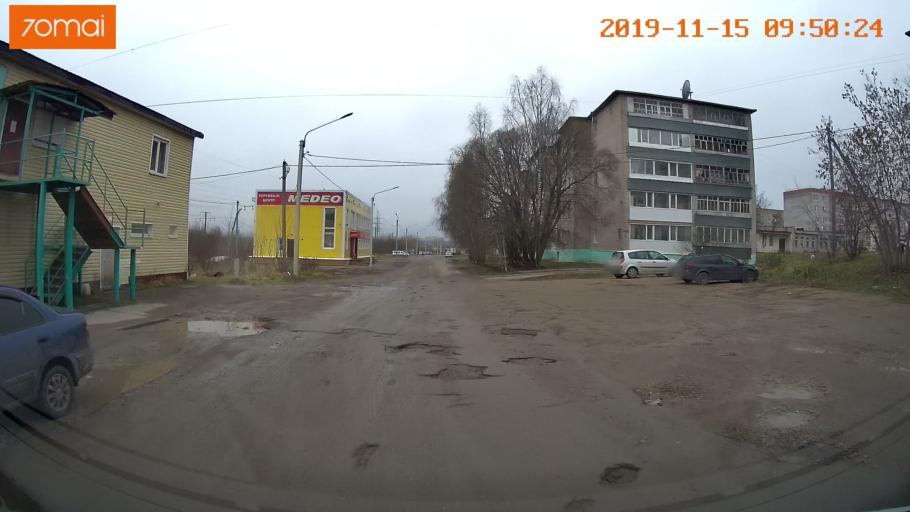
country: RU
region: Vologda
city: Sheksna
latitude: 59.2326
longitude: 38.5126
